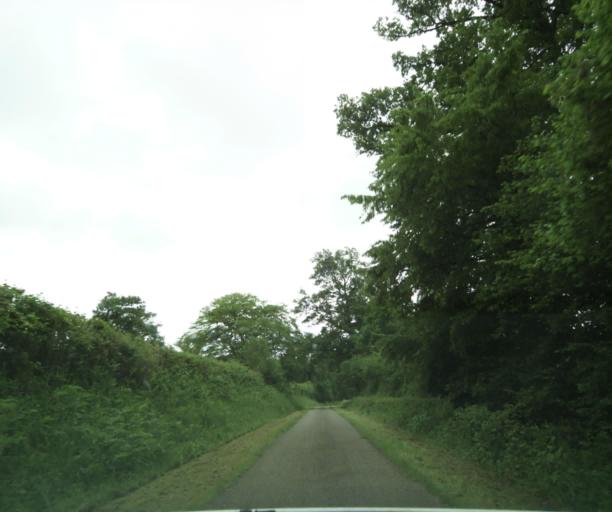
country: FR
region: Bourgogne
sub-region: Departement de Saone-et-Loire
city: Charolles
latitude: 46.4669
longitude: 4.2902
